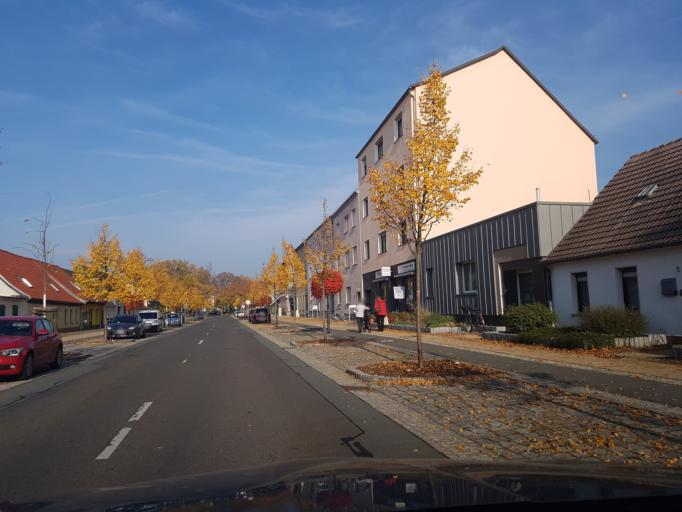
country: DE
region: Brandenburg
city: Elsterwerda
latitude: 51.4605
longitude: 13.5214
